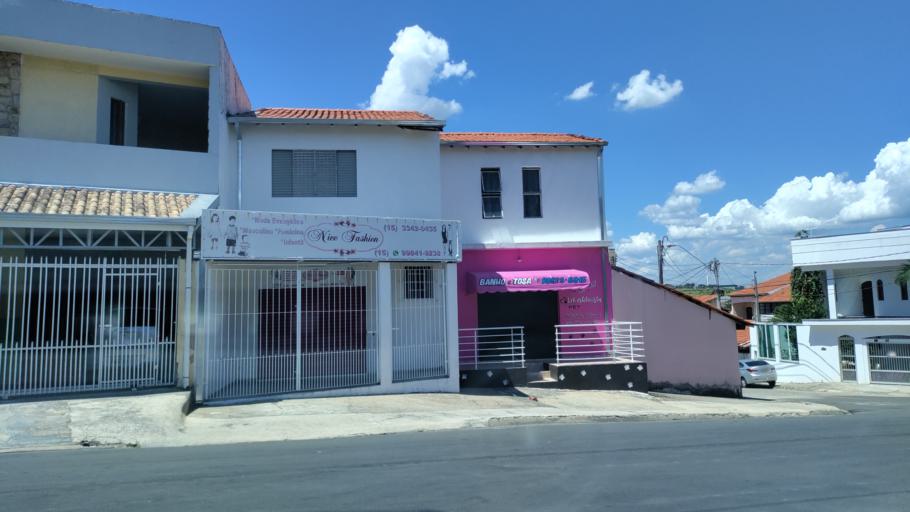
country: BR
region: Sao Paulo
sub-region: Sorocaba
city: Sorocaba
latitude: -23.4547
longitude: -47.4673
